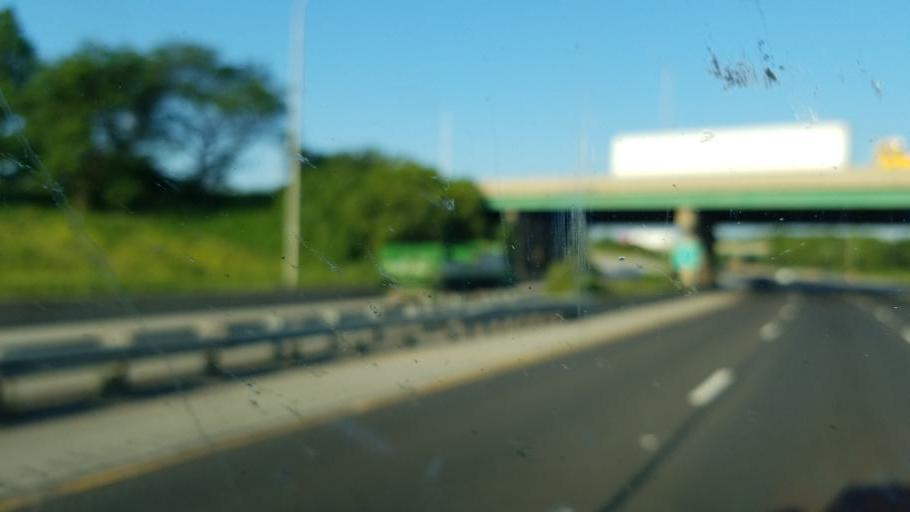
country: US
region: Illinois
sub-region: Cook County
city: Country Club Hills
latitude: 41.5674
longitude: -87.7419
